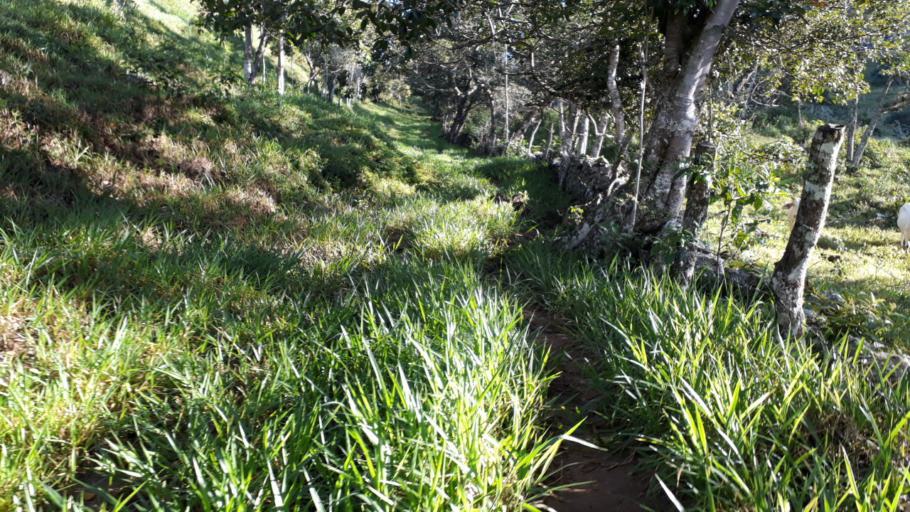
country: CO
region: Casanare
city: Nunchia
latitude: 5.6335
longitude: -72.4246
